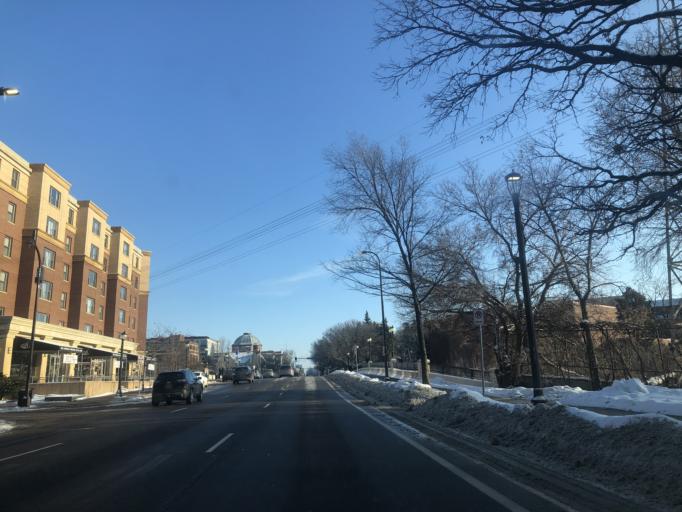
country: US
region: Minnesota
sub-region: Hennepin County
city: Minneapolis
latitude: 44.9801
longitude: -93.2382
